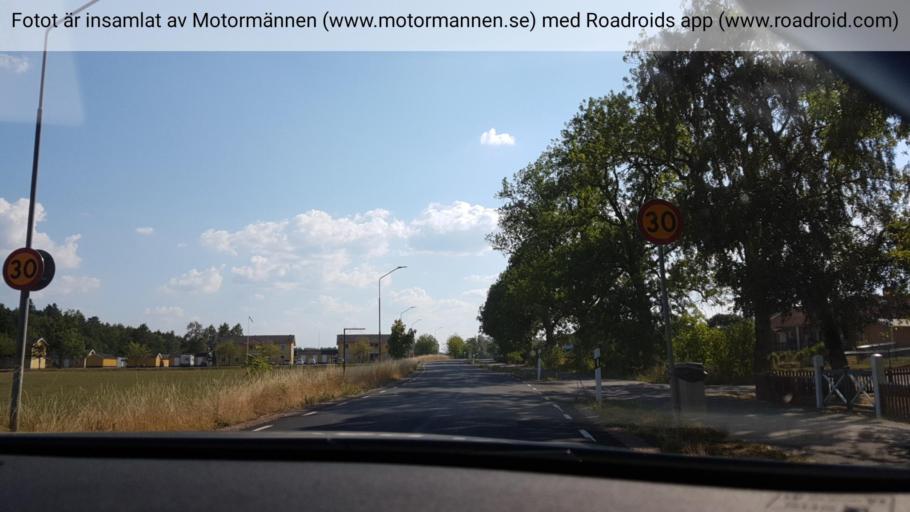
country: SE
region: Vaestra Goetaland
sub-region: Skovde Kommun
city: Stopen
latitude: 58.5812
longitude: 13.8539
